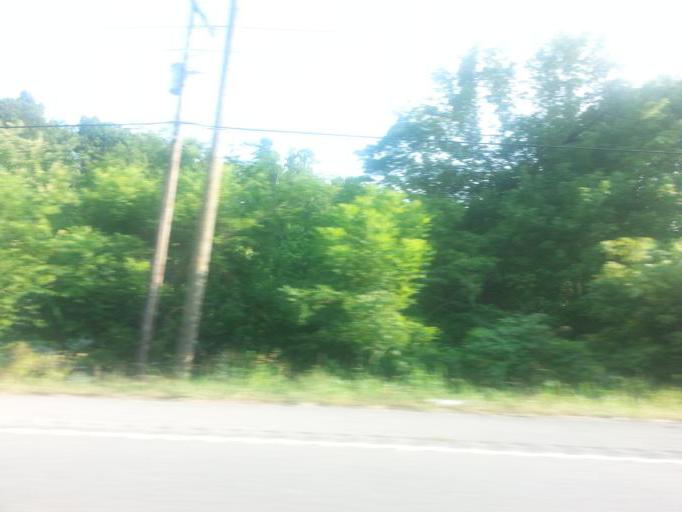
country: US
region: Tennessee
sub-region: Sevier County
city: Sevierville
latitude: 35.8528
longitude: -83.6394
